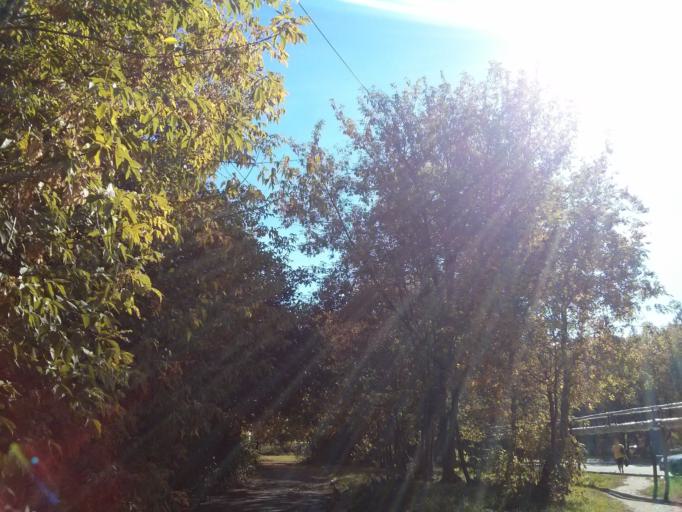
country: RU
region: Vladimir
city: Murom
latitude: 55.5520
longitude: 42.0570
